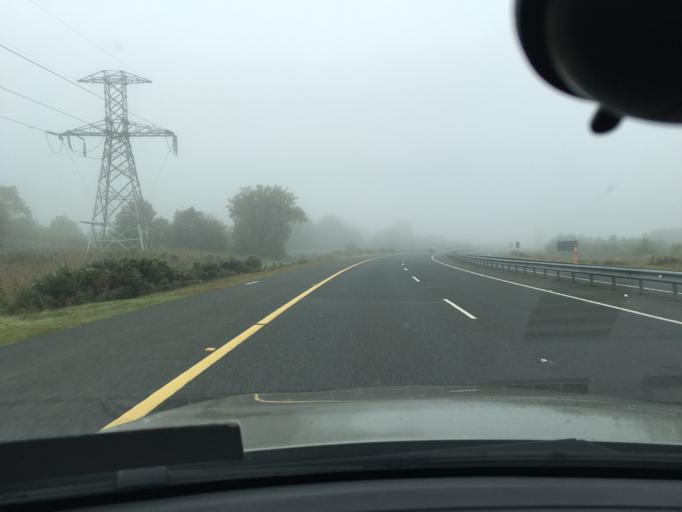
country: IE
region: Leinster
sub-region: An Iarmhi
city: Athlone
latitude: 53.4169
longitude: -7.9863
